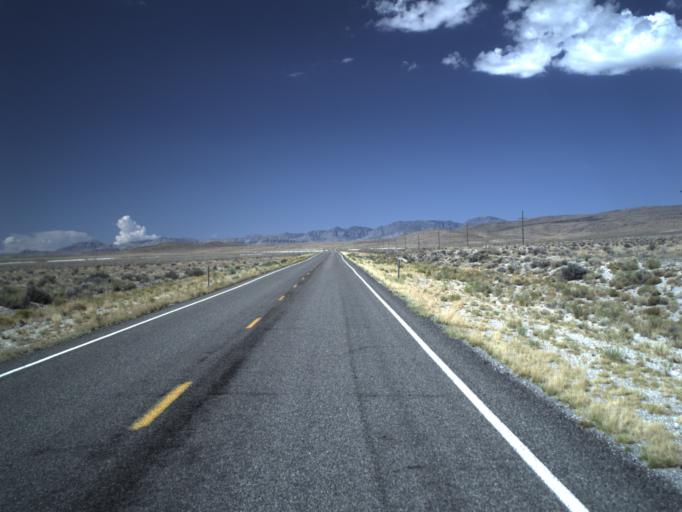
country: US
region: Utah
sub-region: Millard County
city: Delta
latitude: 39.0717
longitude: -113.2186
